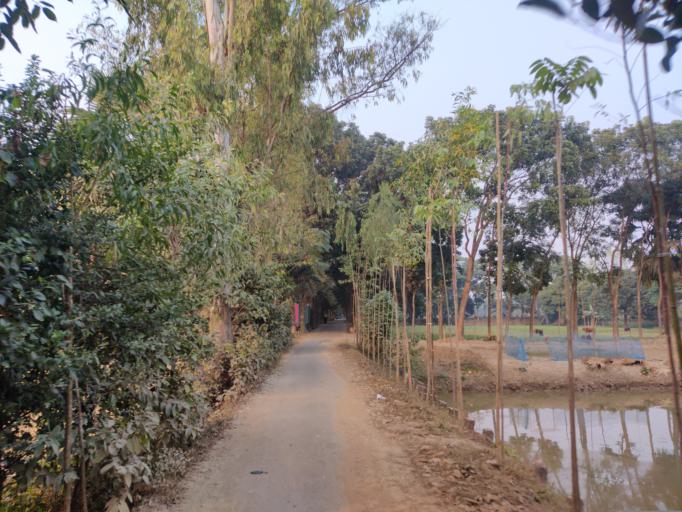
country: BD
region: Dhaka
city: Bajitpur
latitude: 24.1567
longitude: 90.7615
